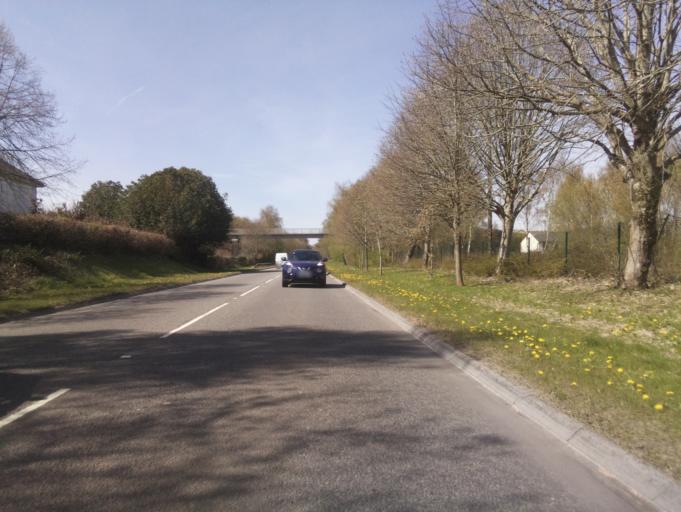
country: GB
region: Wales
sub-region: Rhondda Cynon Taf
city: Aberdare
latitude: 51.7184
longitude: -3.4479
